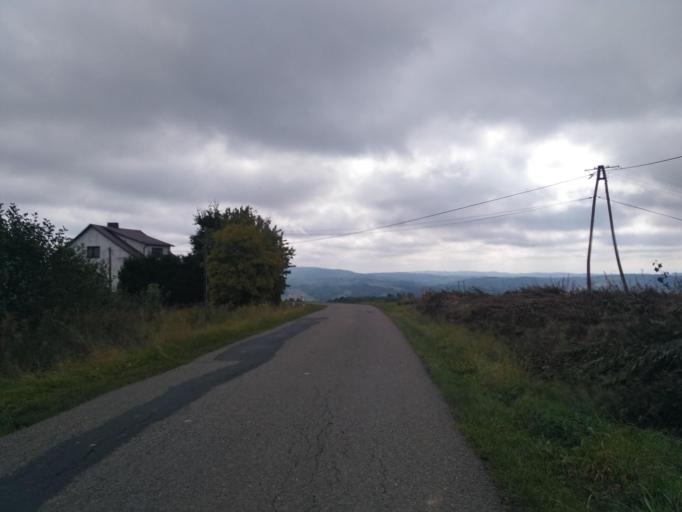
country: PL
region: Subcarpathian Voivodeship
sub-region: Powiat ropczycko-sedziszowski
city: Niedzwiada
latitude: 49.9552
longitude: 21.4554
